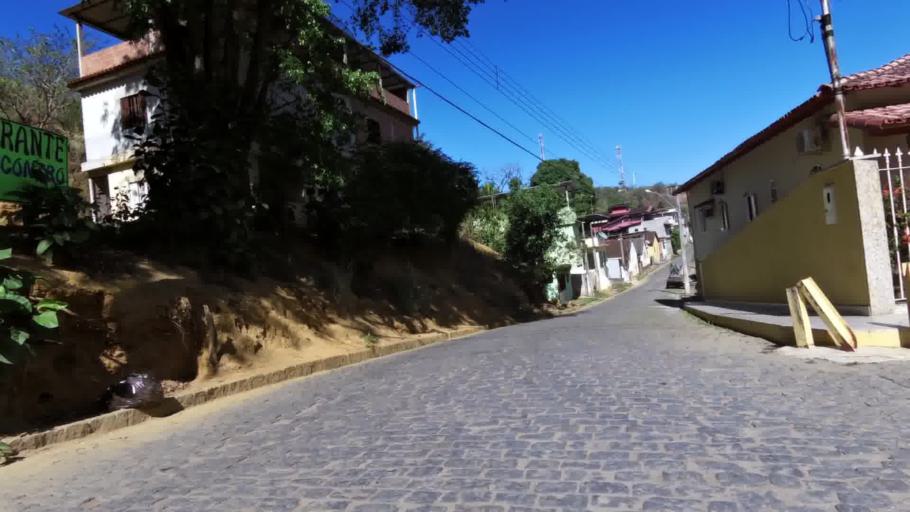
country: BR
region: Espirito Santo
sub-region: Rio Novo Do Sul
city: Rio Novo do Sul
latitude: -20.8650
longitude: -40.9293
